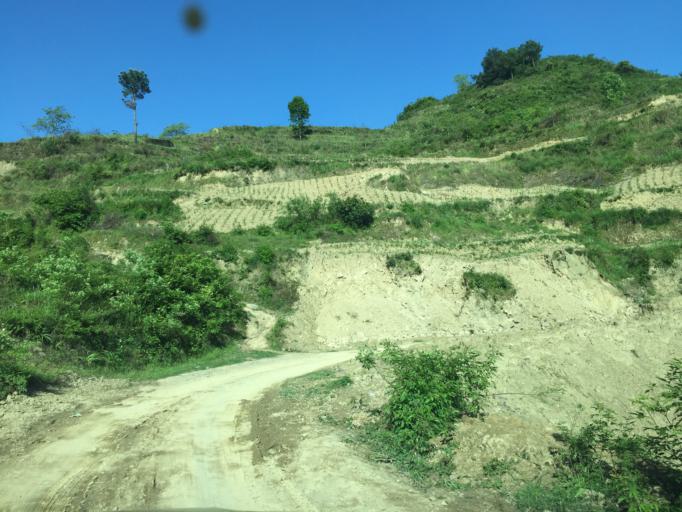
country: CN
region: Guizhou Sheng
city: Xujiaba
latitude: 27.7274
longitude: 108.0247
